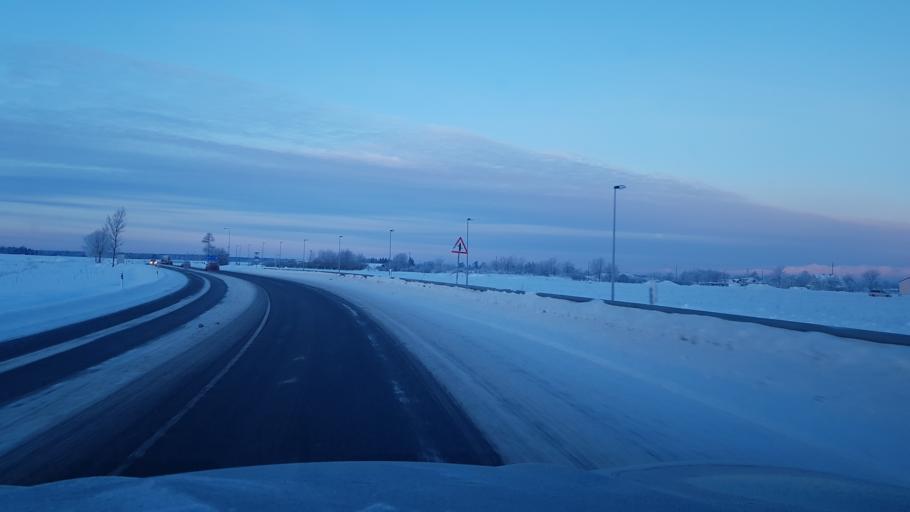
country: EE
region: Ida-Virumaa
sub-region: Narva linn
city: Narva
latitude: 59.3894
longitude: 28.1363
